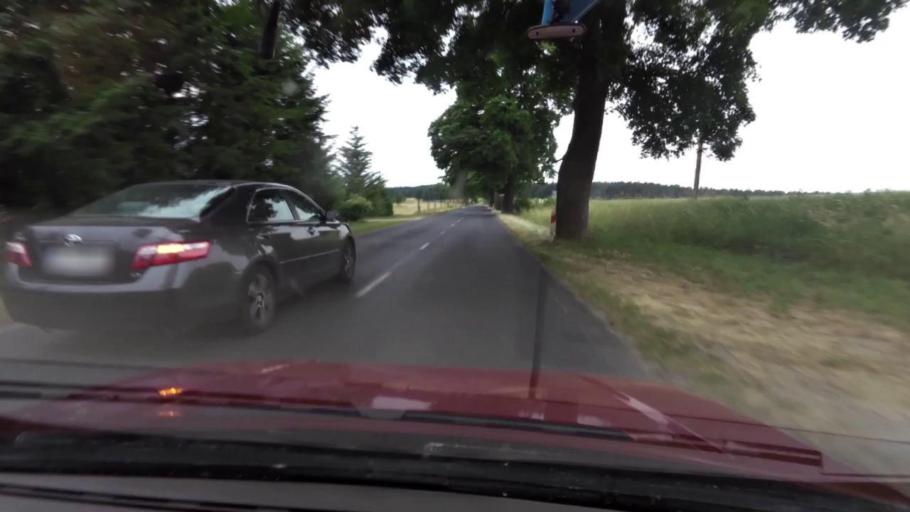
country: PL
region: West Pomeranian Voivodeship
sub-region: Powiat koszalinski
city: Sianow
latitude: 54.1659
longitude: 16.4369
